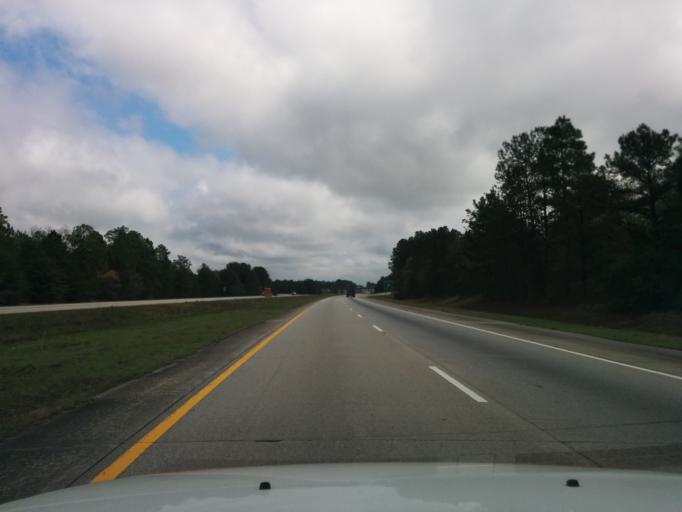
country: US
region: Georgia
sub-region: Emanuel County
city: Swainsboro
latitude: 32.4198
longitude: -82.4000
